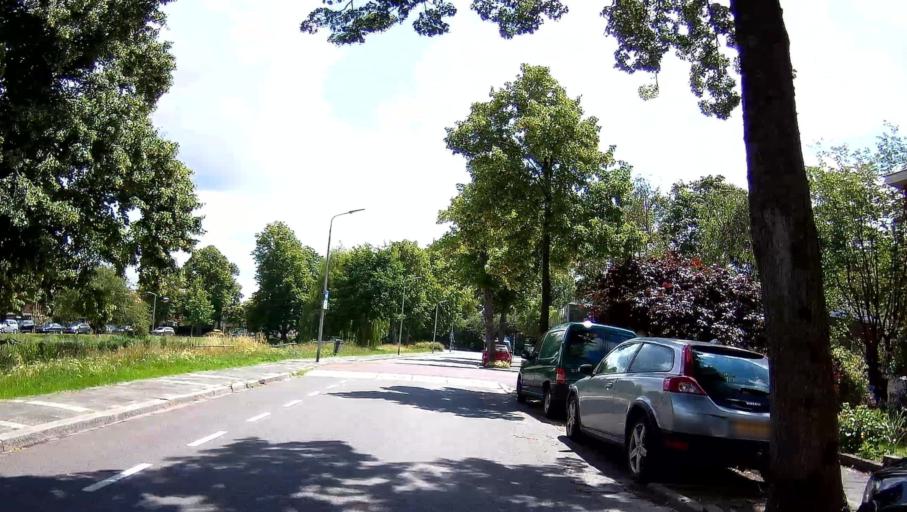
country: NL
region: South Holland
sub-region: Gemeente Delft
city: Delft
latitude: 52.0118
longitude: 4.3451
